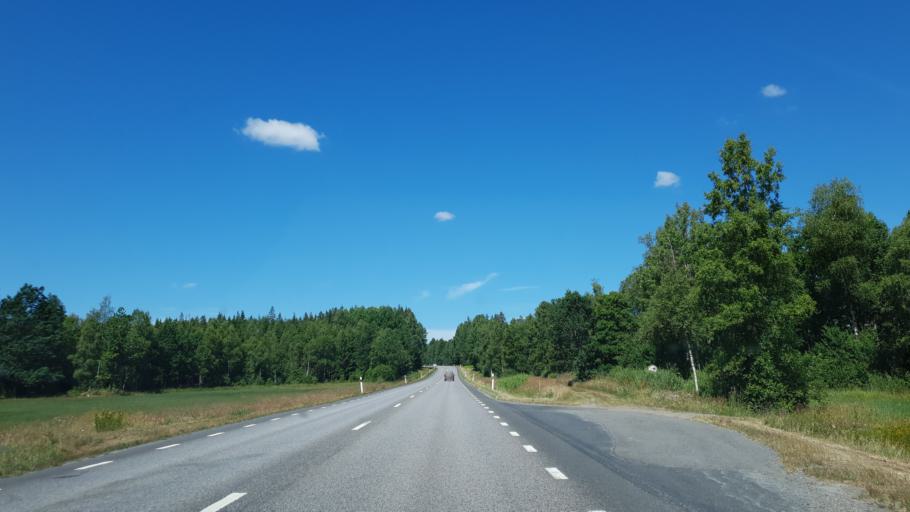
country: SE
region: Joenkoeping
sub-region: Varnamo Kommun
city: Bor
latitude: 57.1361
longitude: 14.1164
